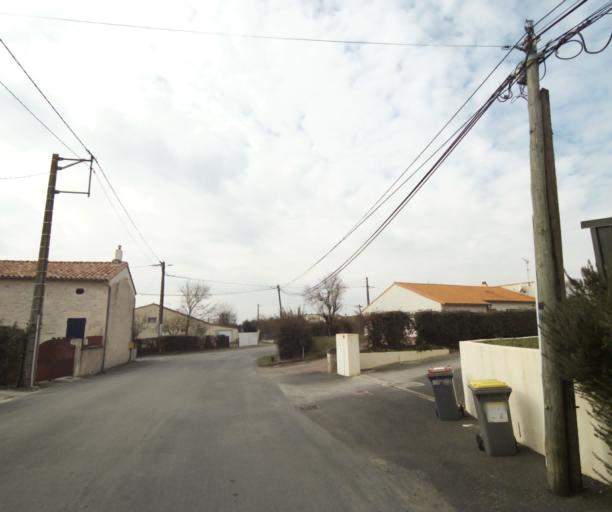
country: FR
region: Poitou-Charentes
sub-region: Departement des Deux-Sevres
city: Saint-Symphorien
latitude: 46.2889
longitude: -0.4716
